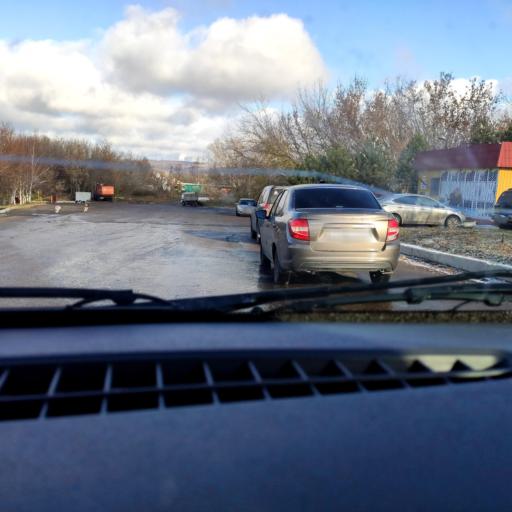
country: RU
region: Bashkortostan
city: Ufa
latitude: 54.8309
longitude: 56.0668
